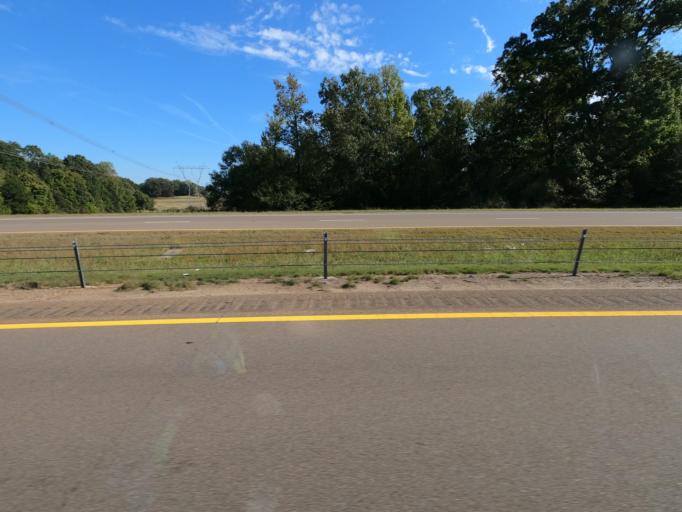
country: US
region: Tennessee
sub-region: Shelby County
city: Arlington
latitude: 35.3057
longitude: -89.6986
